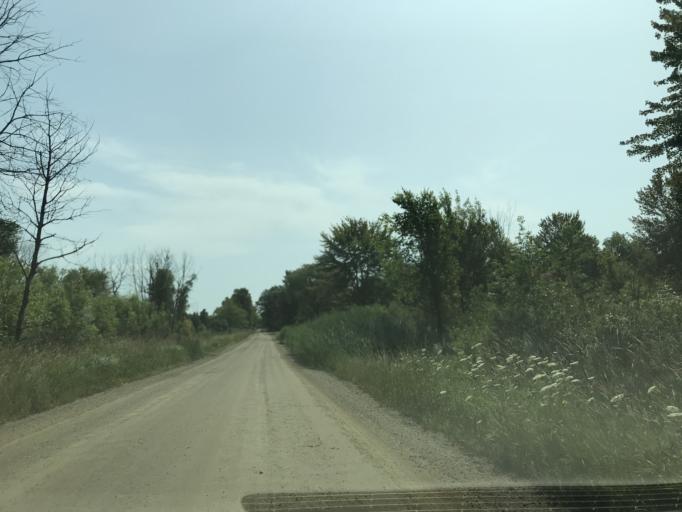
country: US
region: Michigan
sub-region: Eaton County
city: Grand Ledge
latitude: 42.7700
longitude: -84.7065
